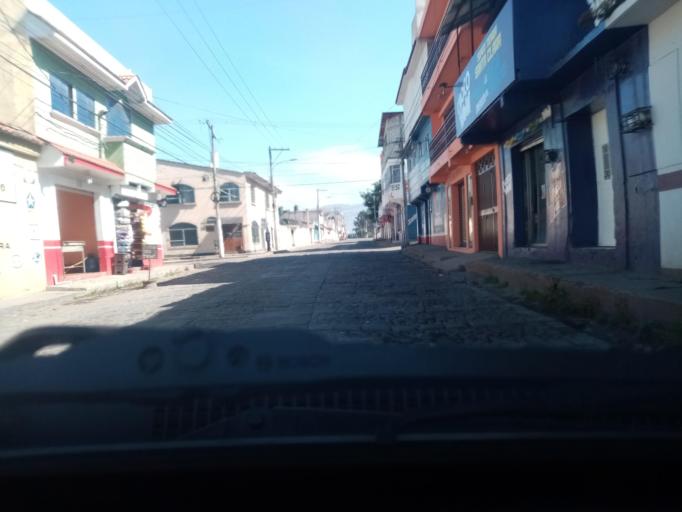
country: GT
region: Quetzaltenango
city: Quetzaltenango
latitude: 14.8440
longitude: -91.5140
